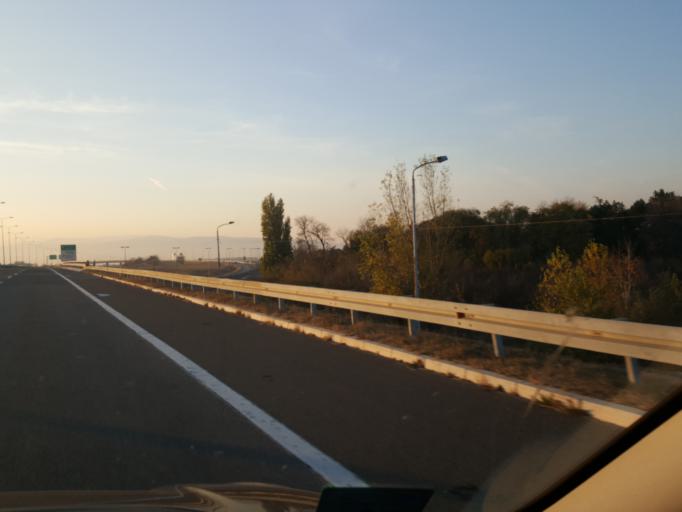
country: RS
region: Central Serbia
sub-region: Nisavski Okrug
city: Nis
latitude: 43.3477
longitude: 21.8650
